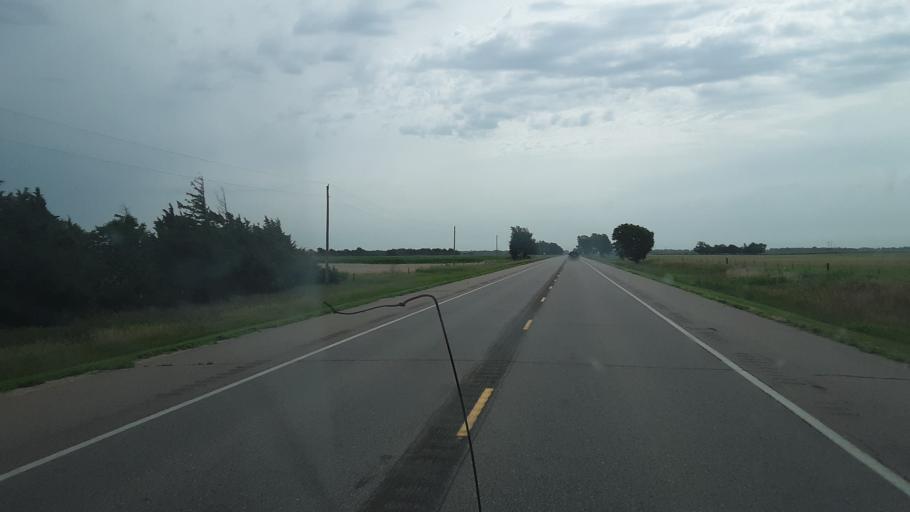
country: US
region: Kansas
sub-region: Stafford County
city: Saint John
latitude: 37.9559
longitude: -98.7655
